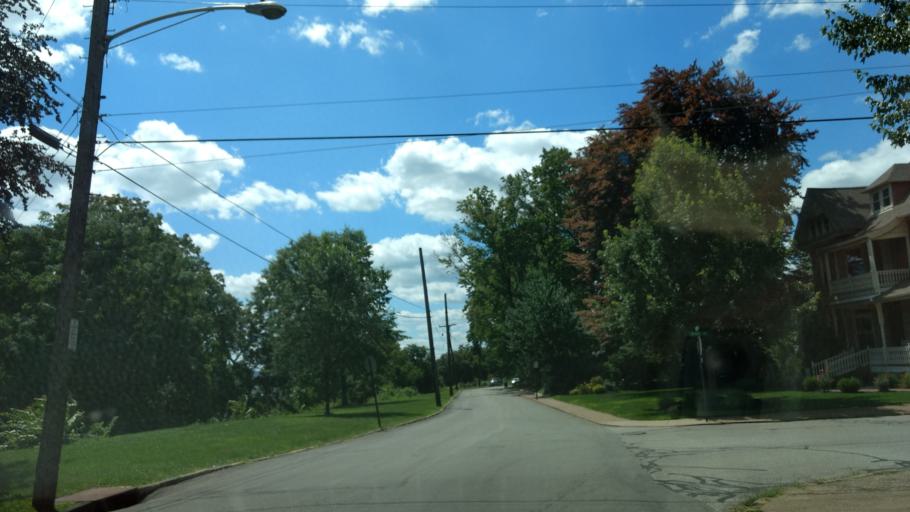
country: US
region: Pennsylvania
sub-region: Beaver County
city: Beaver
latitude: 40.6898
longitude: -80.3073
